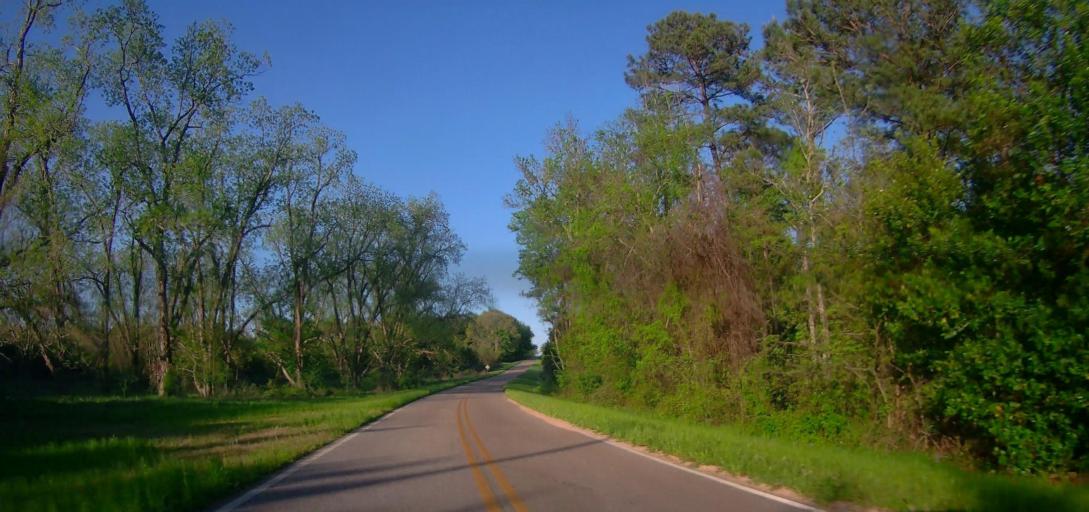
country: US
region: Georgia
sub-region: Macon County
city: Oglethorpe
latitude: 32.2999
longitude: -84.1423
